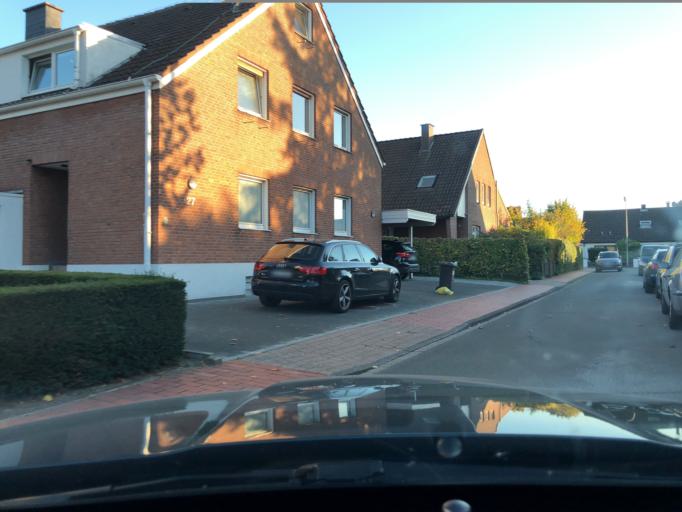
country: DE
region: North Rhine-Westphalia
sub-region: Regierungsbezirk Munster
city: Telgte
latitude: 51.9861
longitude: 7.7050
